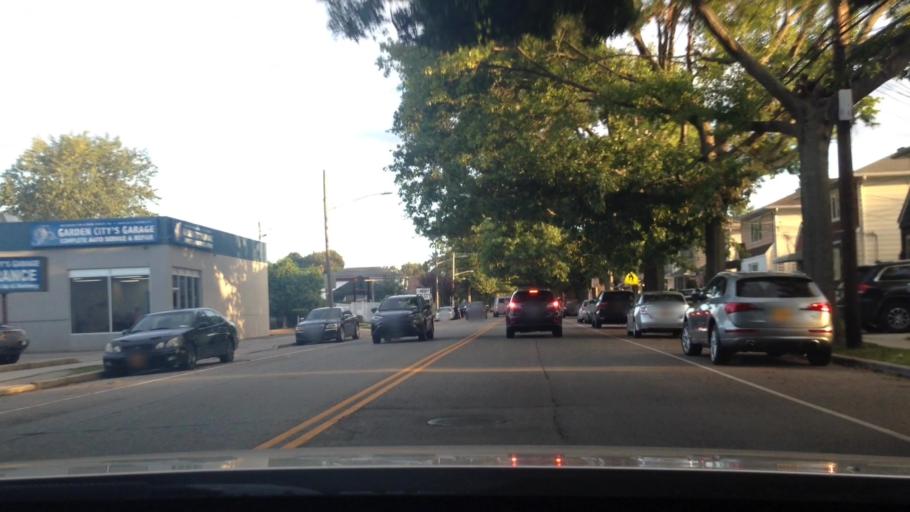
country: US
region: New York
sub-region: Nassau County
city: Garden City South
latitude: 40.7111
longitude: -73.6610
